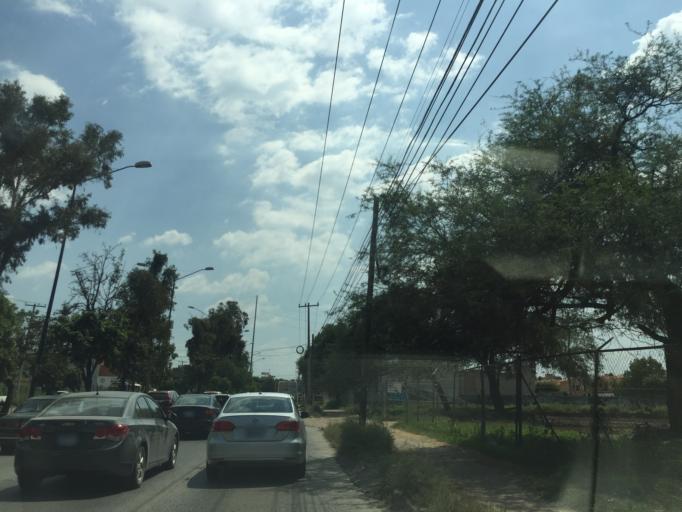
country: MX
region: Guanajuato
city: Leon
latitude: 21.1535
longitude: -101.6691
